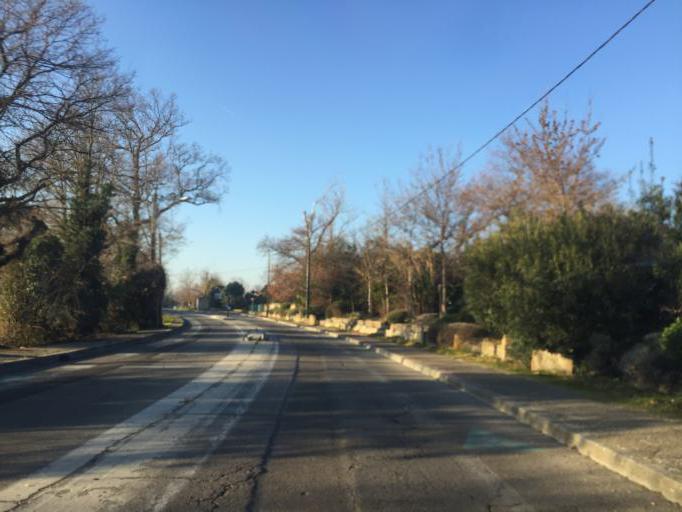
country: FR
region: Provence-Alpes-Cote d'Azur
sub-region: Departement du Vaucluse
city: Montfavet
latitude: 43.9395
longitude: 4.8701
